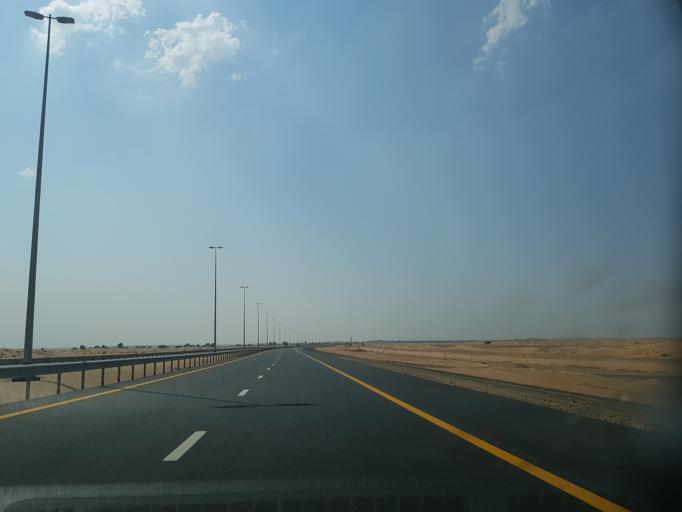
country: AE
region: Ash Shariqah
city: Adh Dhayd
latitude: 25.2594
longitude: 55.6898
